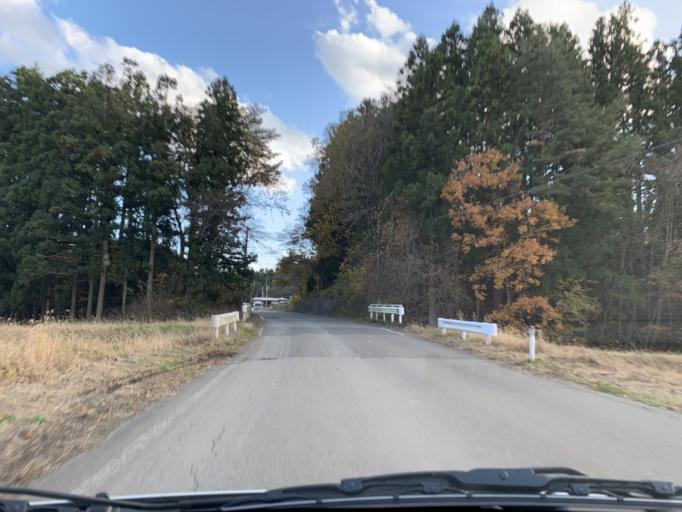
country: JP
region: Iwate
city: Mizusawa
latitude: 39.1181
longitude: 141.0369
